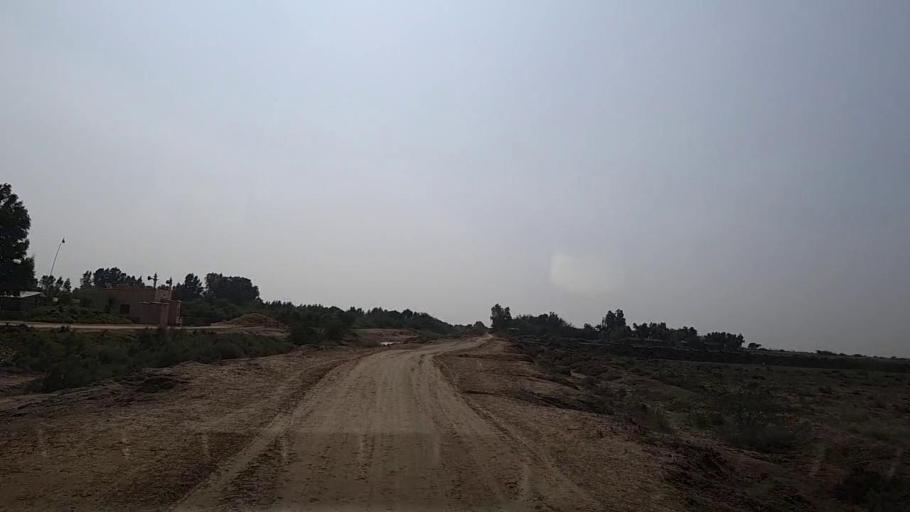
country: PK
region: Sindh
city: Mirpur Sakro
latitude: 24.5496
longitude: 67.7911
